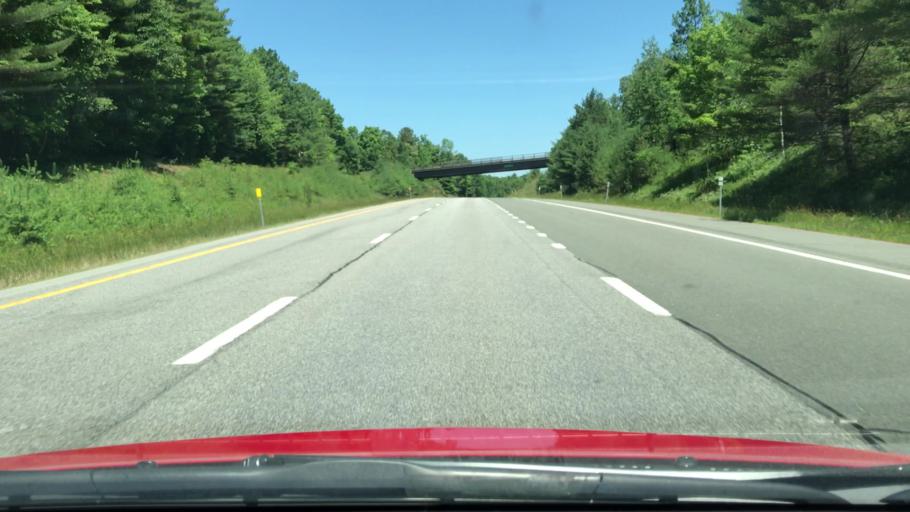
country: US
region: New York
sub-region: Essex County
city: Elizabethtown
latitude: 44.1659
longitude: -73.5837
